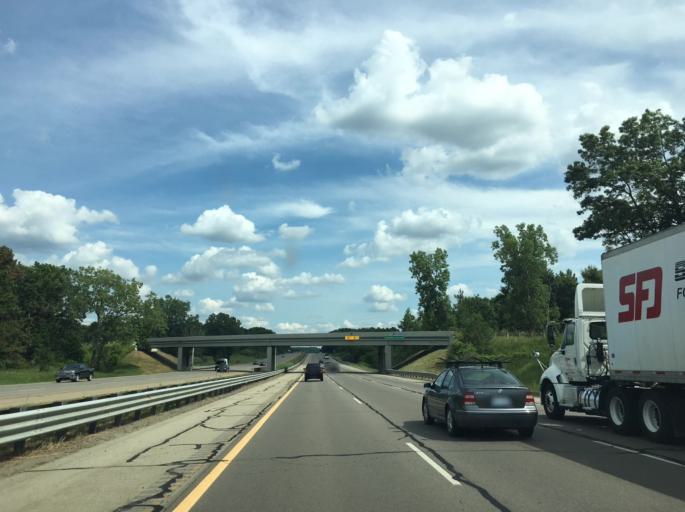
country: US
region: Michigan
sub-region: Oakland County
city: Holly
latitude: 42.7736
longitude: -83.5253
